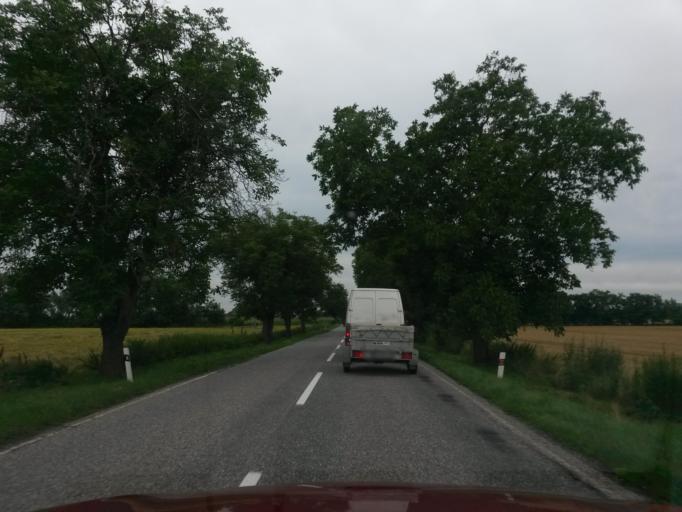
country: SK
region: Nitriansky
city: Levice
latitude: 48.1415
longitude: 18.5837
